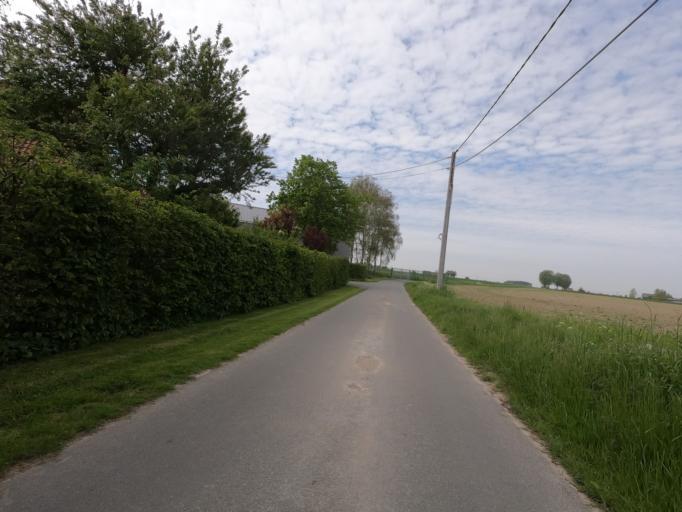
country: BE
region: Flanders
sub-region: Provincie West-Vlaanderen
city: Alveringem
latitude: 50.9666
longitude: 2.6934
